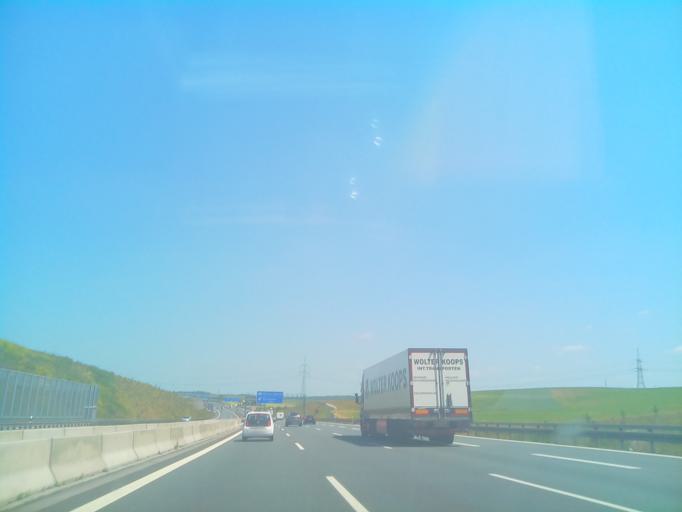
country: DE
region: Bavaria
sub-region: Regierungsbezirk Unterfranken
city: Theilheim
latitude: 49.7514
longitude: 10.0421
